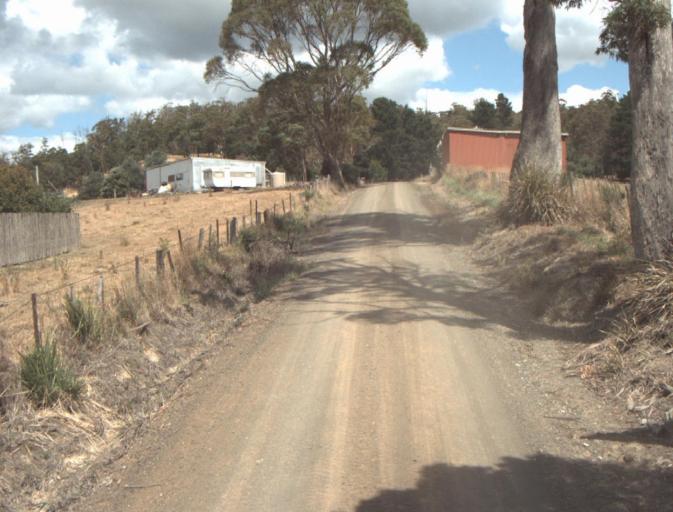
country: AU
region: Tasmania
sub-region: Launceston
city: Mayfield
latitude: -41.2343
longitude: 147.1255
